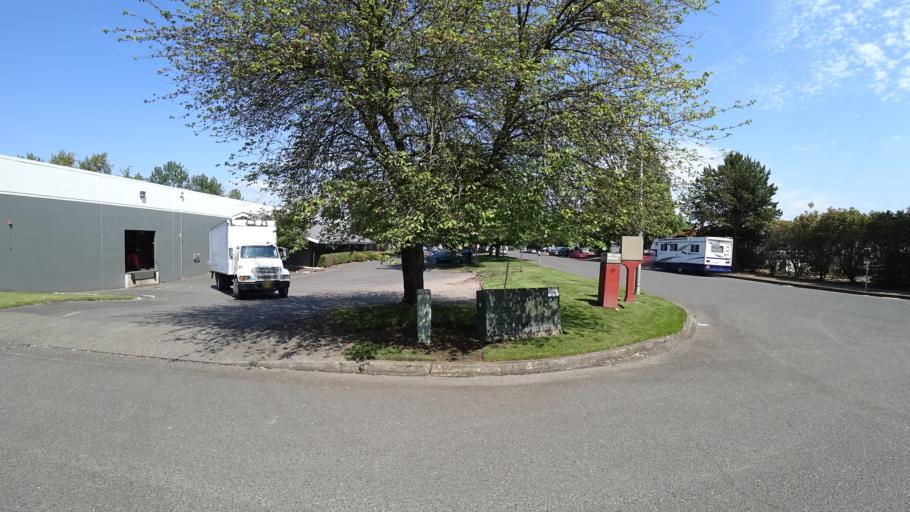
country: US
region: Oregon
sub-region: Multnomah County
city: Lents
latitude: 45.5613
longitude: -122.5442
